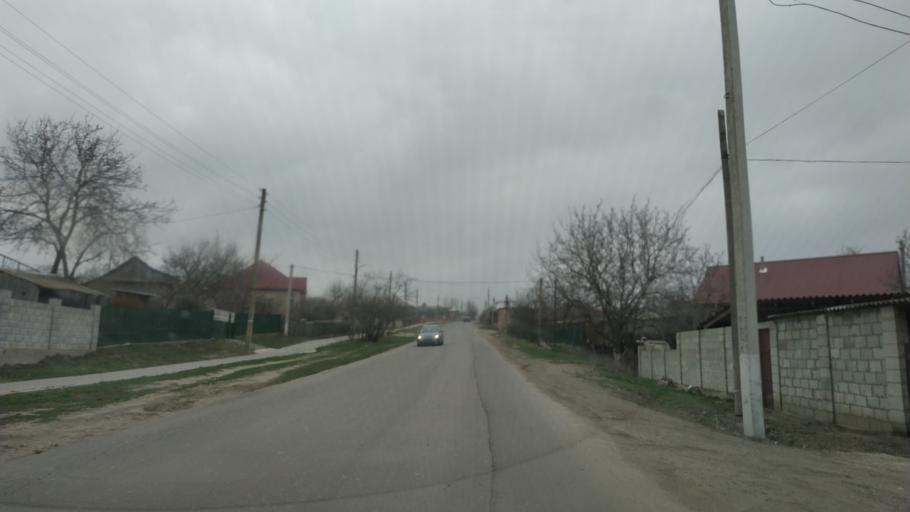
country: MD
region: Gagauzia
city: Comrat
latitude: 46.2877
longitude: 28.6703
